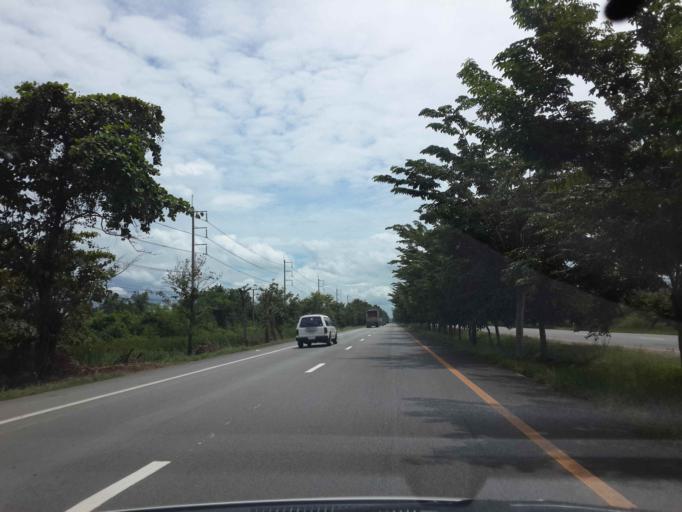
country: TH
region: Ratchaburi
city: Pak Tho
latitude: 13.4022
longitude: 99.8140
